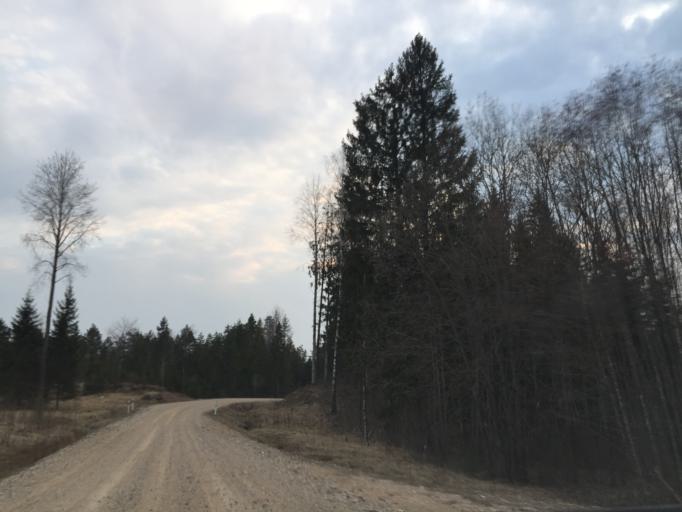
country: LV
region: Raunas
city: Rauna
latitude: 57.1299
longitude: 25.5992
